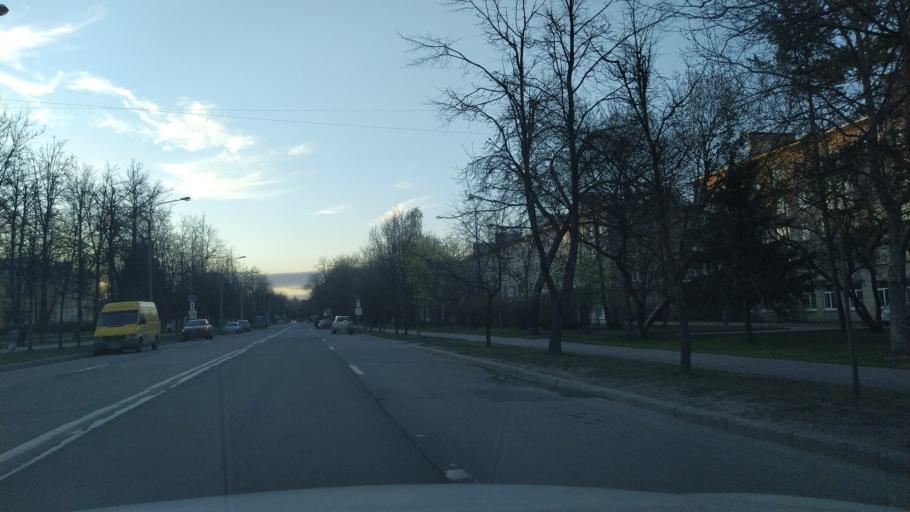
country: RU
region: St.-Petersburg
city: Pushkin
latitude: 59.7046
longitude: 30.4064
